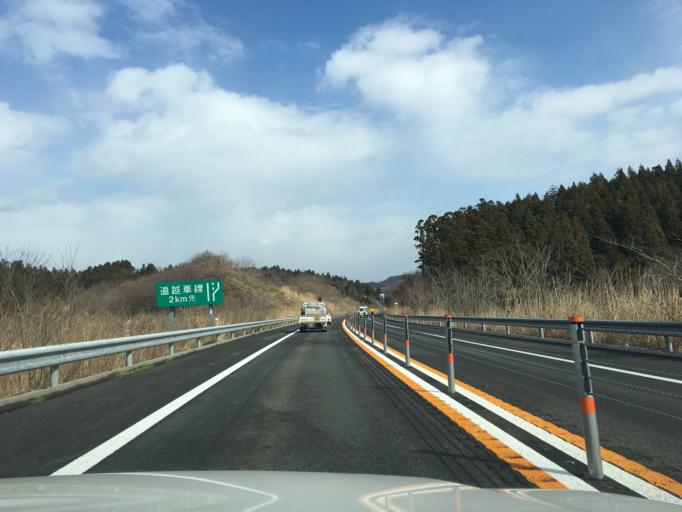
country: JP
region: Akita
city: Akita Shi
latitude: 39.4818
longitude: 140.0529
